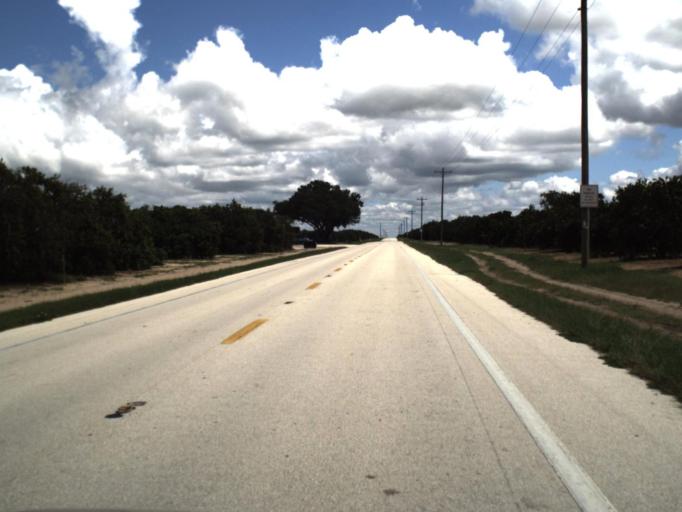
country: US
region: Florida
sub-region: Polk County
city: Fort Meade
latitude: 27.7335
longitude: -81.7139
